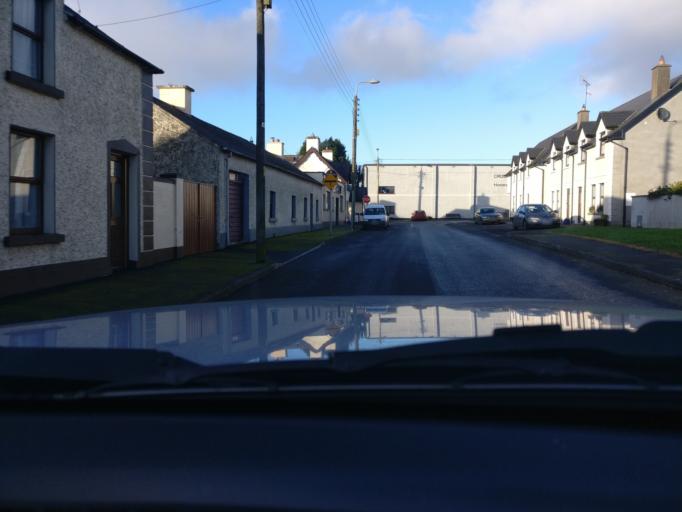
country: IE
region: Ulster
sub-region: An Cabhan
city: Mullagh
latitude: 53.7142
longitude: -7.0197
